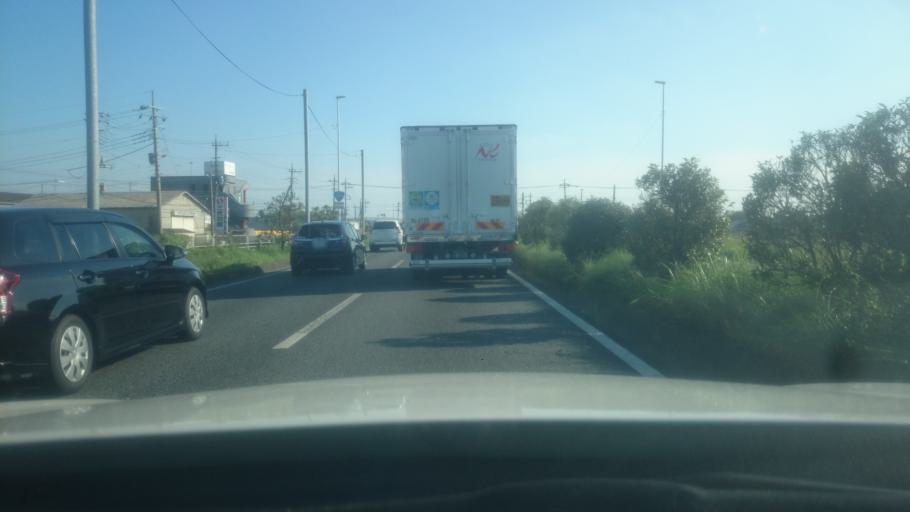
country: JP
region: Saitama
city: Kawagoe
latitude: 35.9059
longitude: 139.5056
